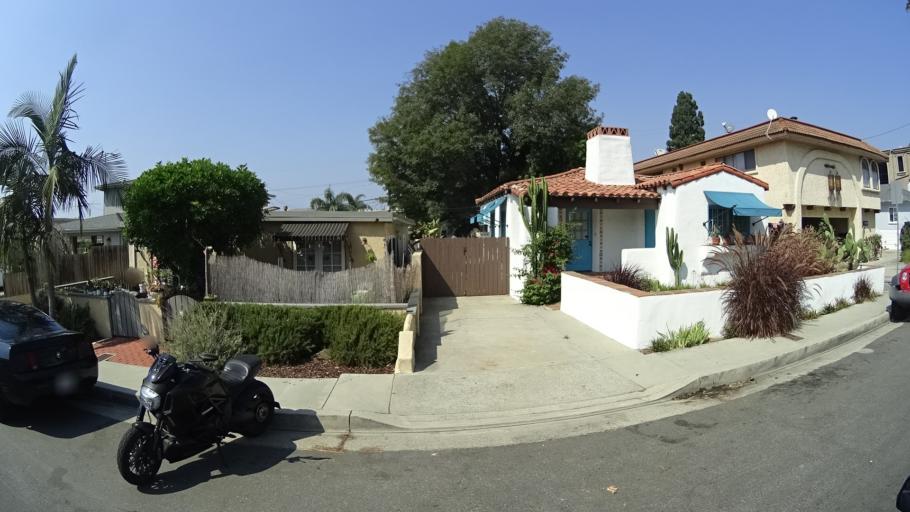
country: US
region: California
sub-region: Orange County
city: San Clemente
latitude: 33.4270
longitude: -117.6194
